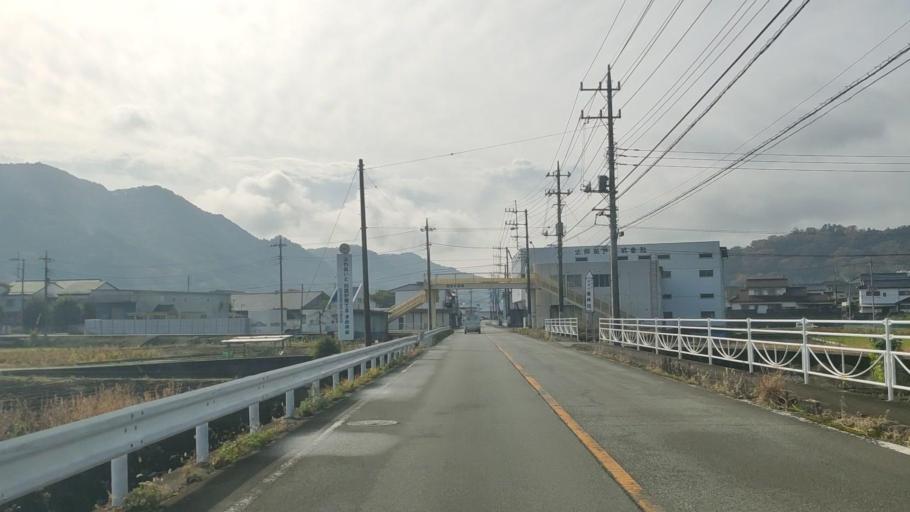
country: JP
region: Yamanashi
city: Ryuo
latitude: 35.4901
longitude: 138.4497
